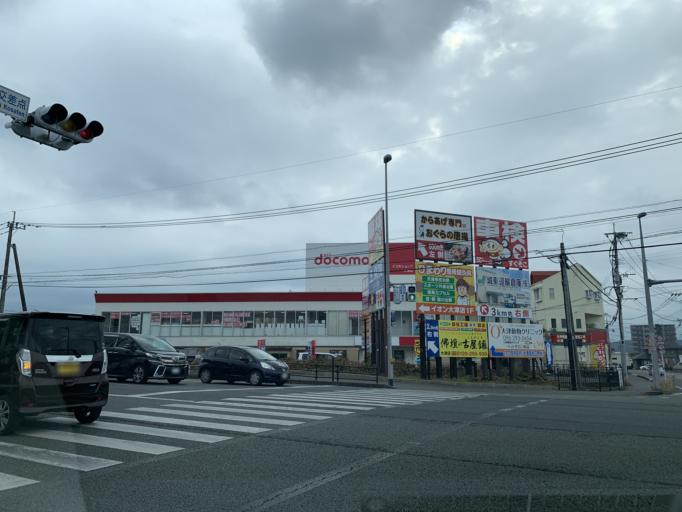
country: JP
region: Kumamoto
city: Ozu
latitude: 32.8756
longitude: 130.8659
